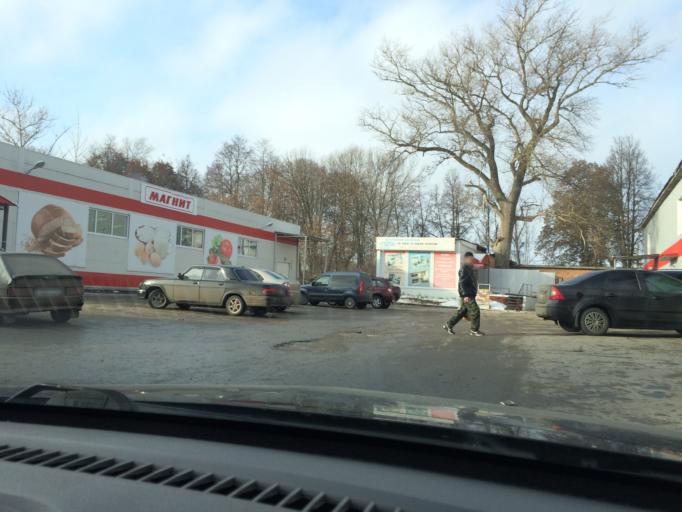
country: RU
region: Tula
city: Plavsk
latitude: 53.7024
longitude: 37.2870
